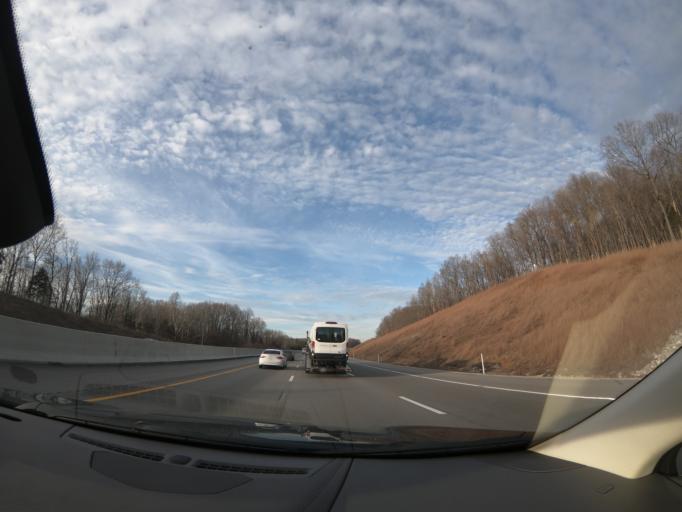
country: US
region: Kentucky
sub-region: Hart County
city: Munfordville
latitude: 37.3357
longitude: -85.9074
